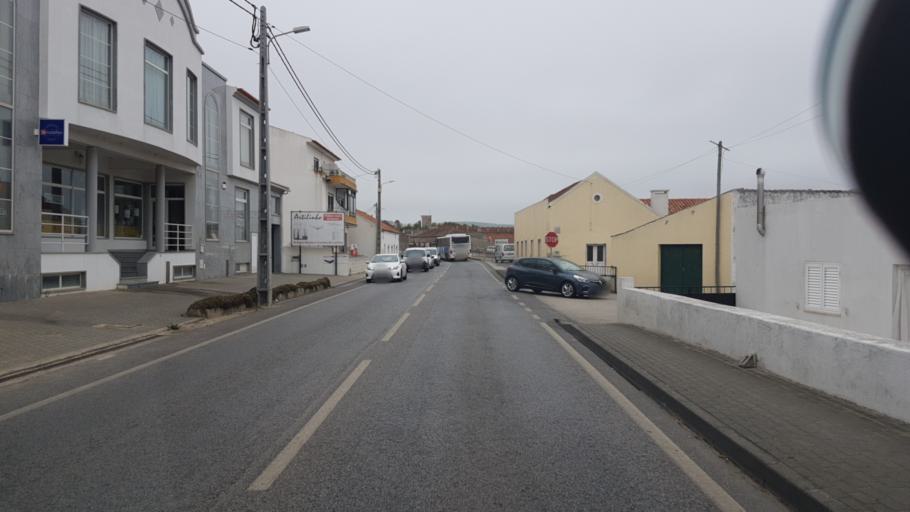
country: PT
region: Lisbon
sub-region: Torres Vedras
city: Silveira
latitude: 39.0889
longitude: -9.3164
